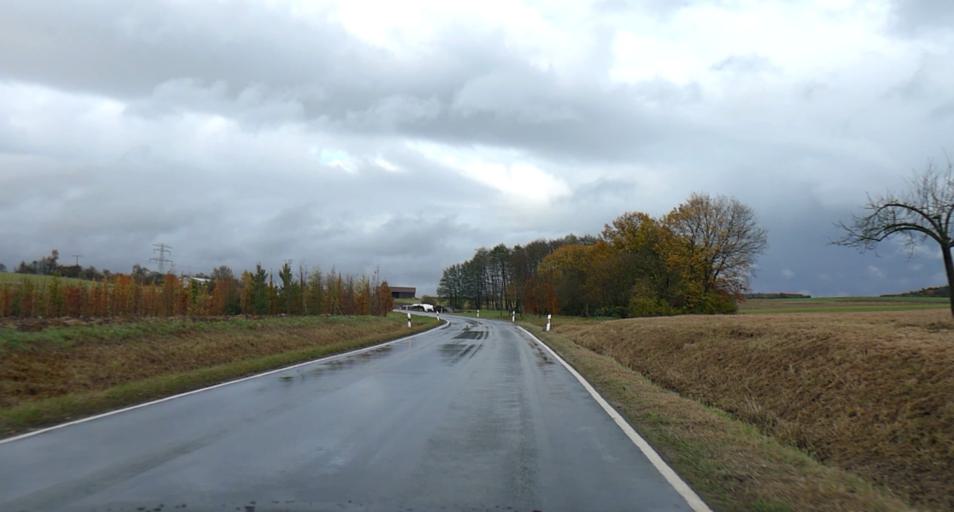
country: DE
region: Bavaria
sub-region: Upper Franconia
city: Effeltrich
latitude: 49.6664
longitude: 11.1156
